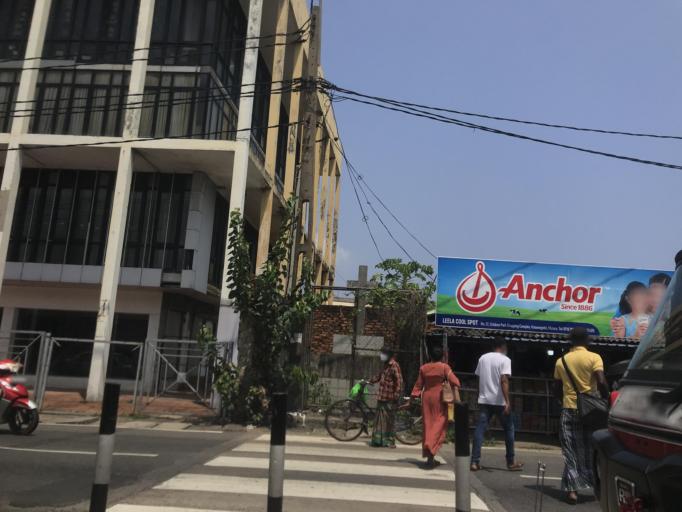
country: LK
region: Southern
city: Matara
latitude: 5.9436
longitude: 80.5496
